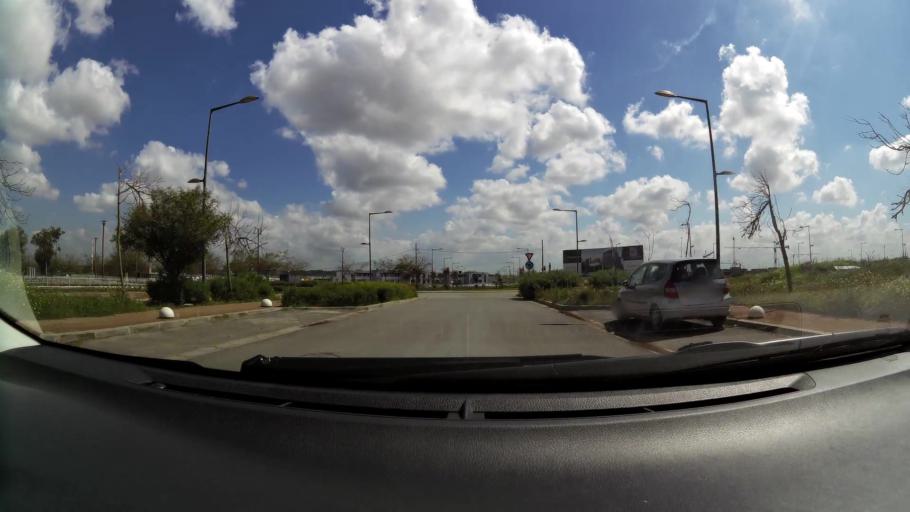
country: MA
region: Grand Casablanca
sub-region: Nouaceur
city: Bouskoura
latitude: 33.4935
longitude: -7.6034
